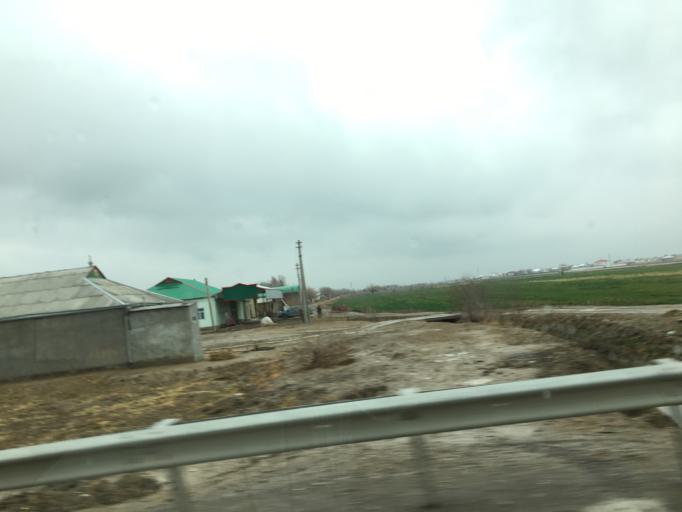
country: TM
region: Mary
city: Yoloeten
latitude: 37.3025
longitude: 62.3267
